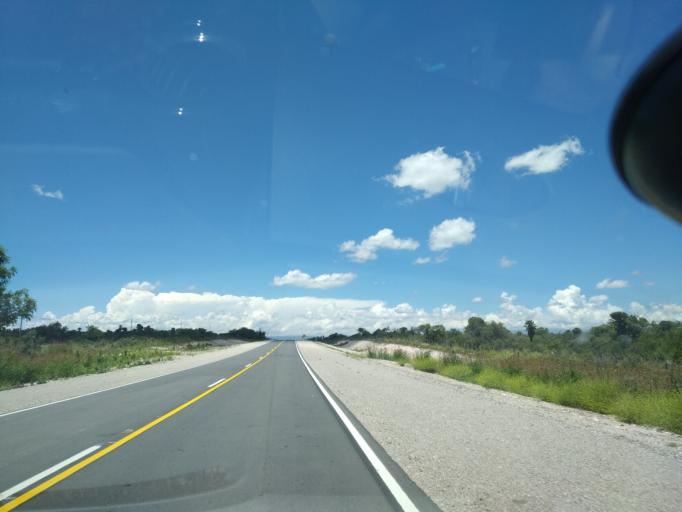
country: AR
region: Cordoba
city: Salsacate
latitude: -31.3719
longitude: -65.2586
